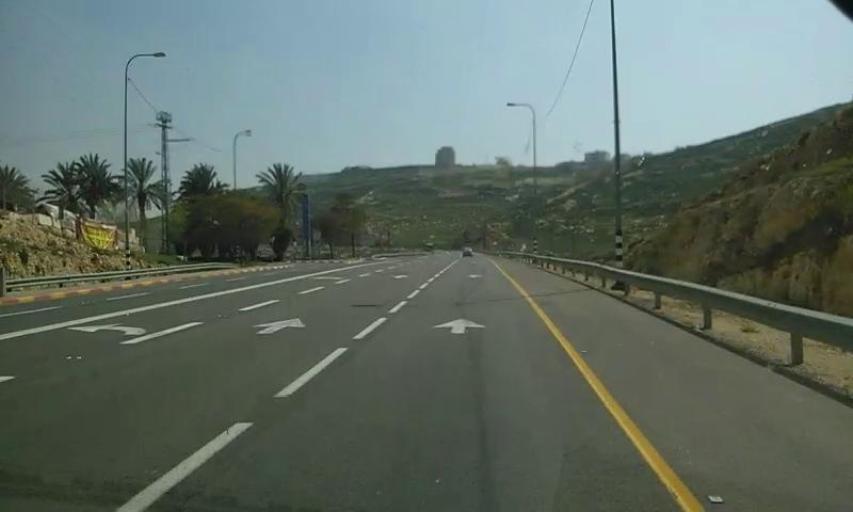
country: PS
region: West Bank
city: Jaba`
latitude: 31.8646
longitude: 35.2593
